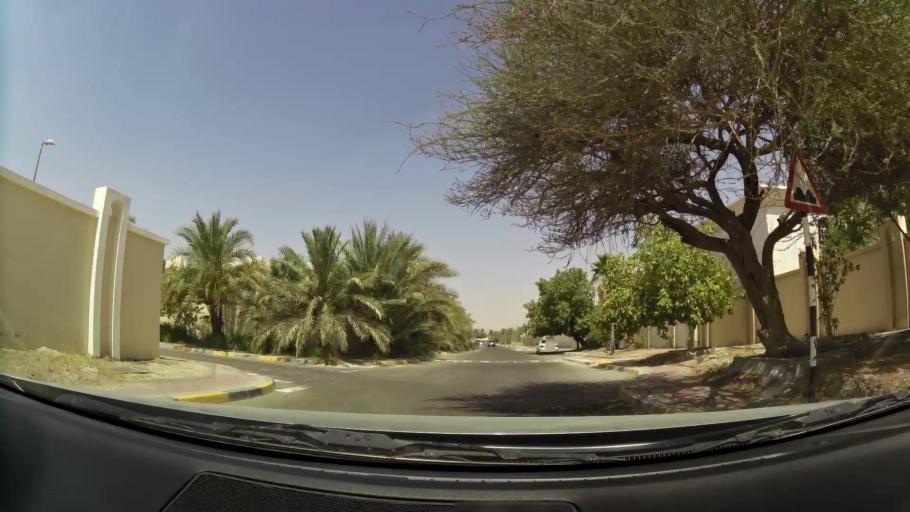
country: OM
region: Al Buraimi
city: Al Buraymi
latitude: 24.2820
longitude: 55.7801
